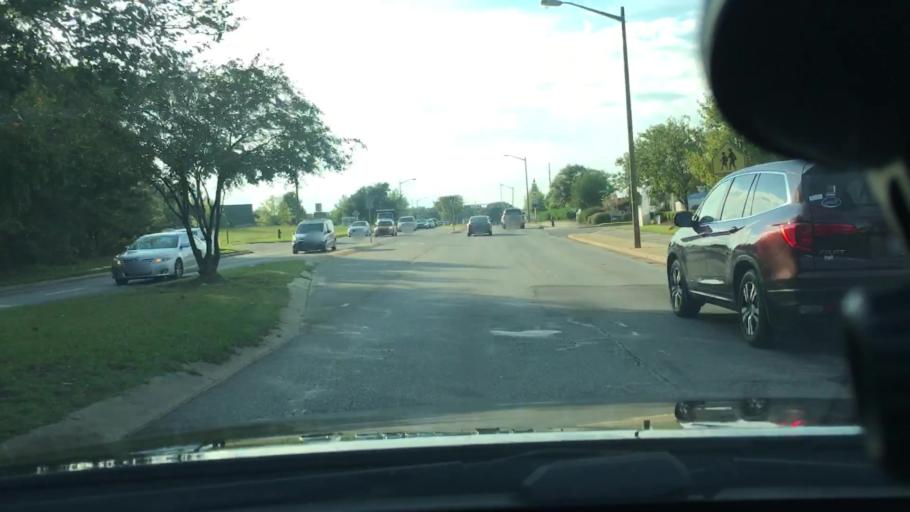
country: US
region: North Carolina
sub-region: Pitt County
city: Greenville
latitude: 35.5913
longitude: -77.3796
